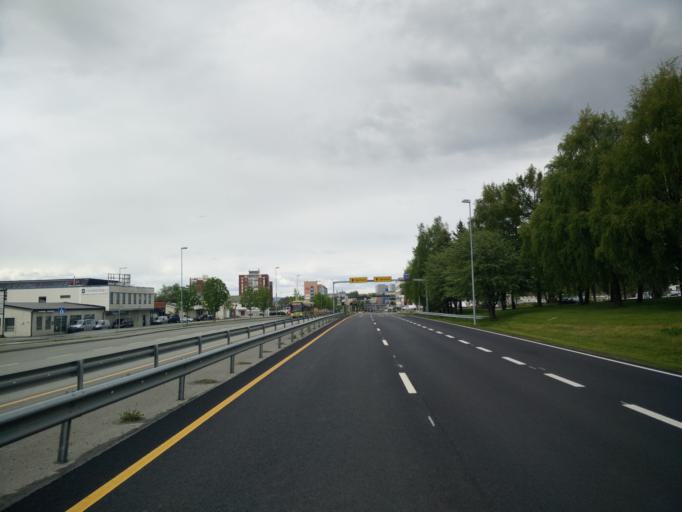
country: NO
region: Sor-Trondelag
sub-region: Trondheim
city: Trondheim
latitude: 63.4029
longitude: 10.3961
